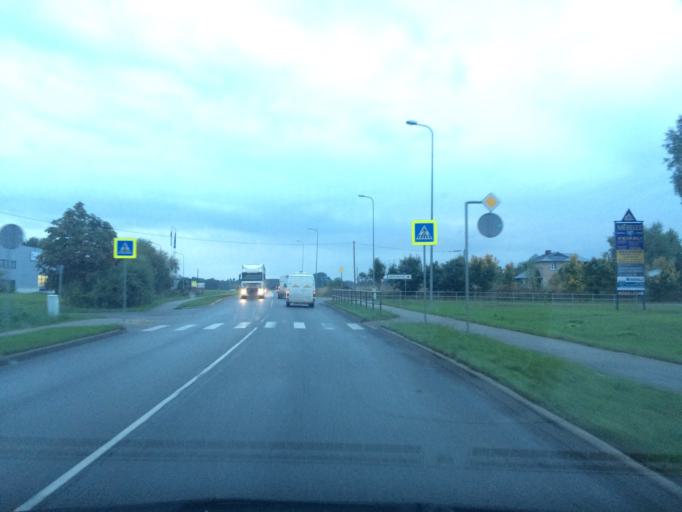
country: LV
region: Jekabpils Rajons
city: Jekabpils
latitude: 56.5221
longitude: 25.8456
